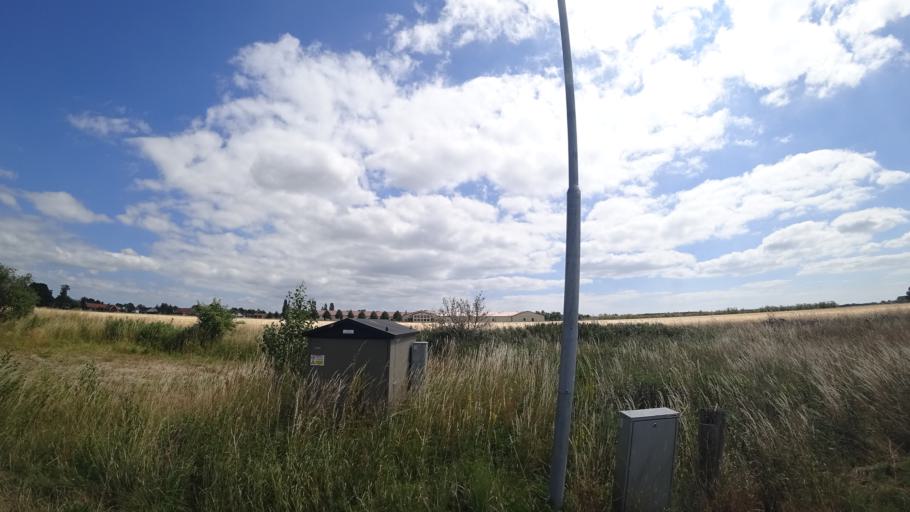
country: SE
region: Skane
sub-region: Kristianstads Kommun
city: Ahus
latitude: 55.9766
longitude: 14.2646
